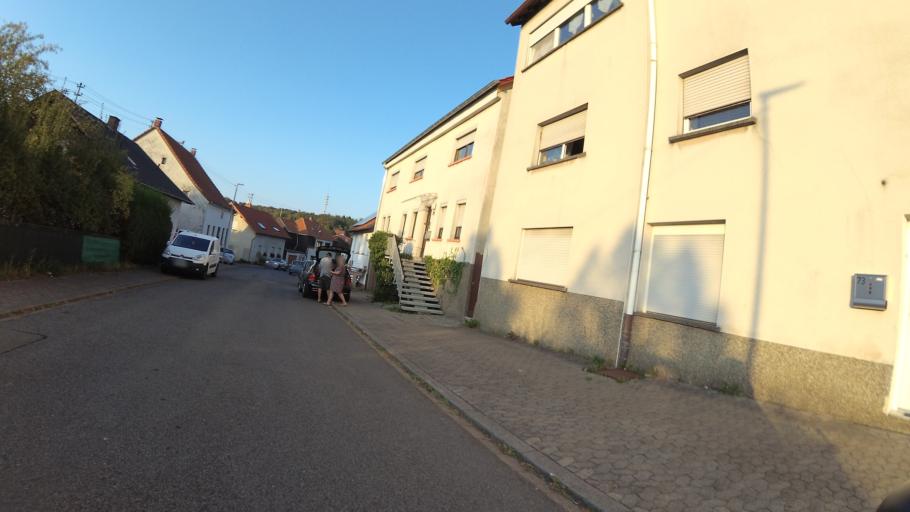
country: DE
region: Saarland
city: Friedrichsthal
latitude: 49.3182
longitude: 7.0977
